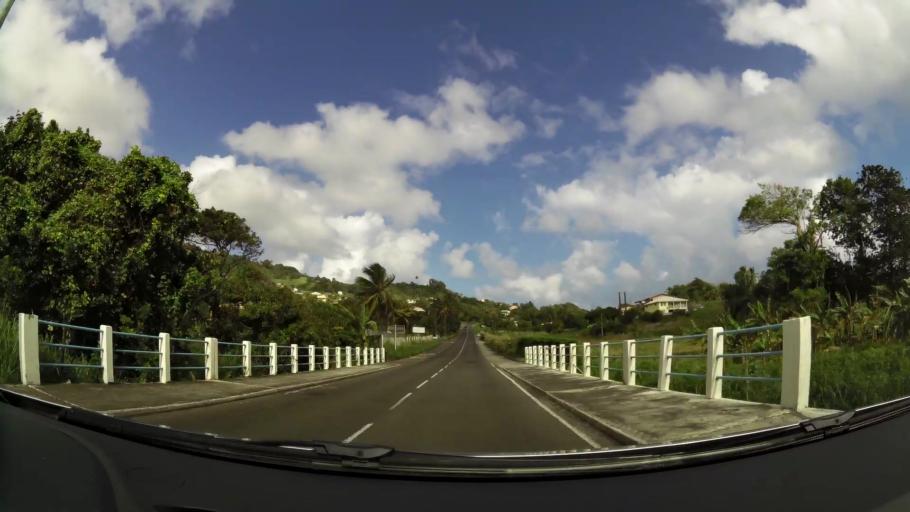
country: MQ
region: Martinique
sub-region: Martinique
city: Sainte-Marie
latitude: 14.8084
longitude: -61.0203
